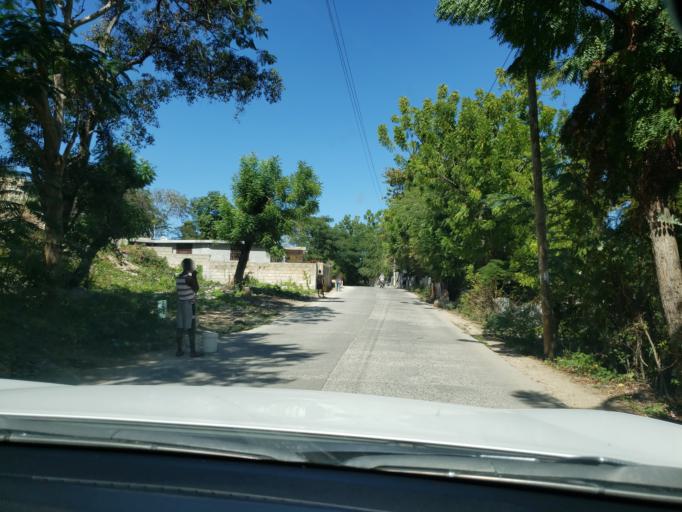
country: HT
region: Nippes
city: Miragoane
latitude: 18.4460
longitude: -73.1055
